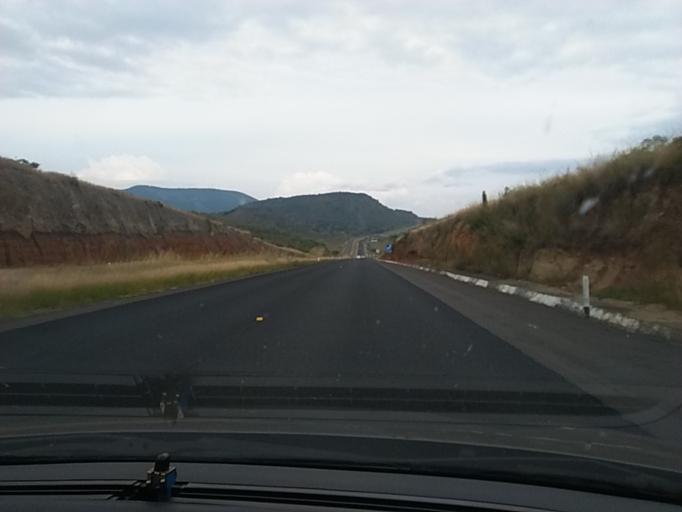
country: MX
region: Mexico
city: Huaniqueo de Morales
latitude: 19.8868
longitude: -101.4724
